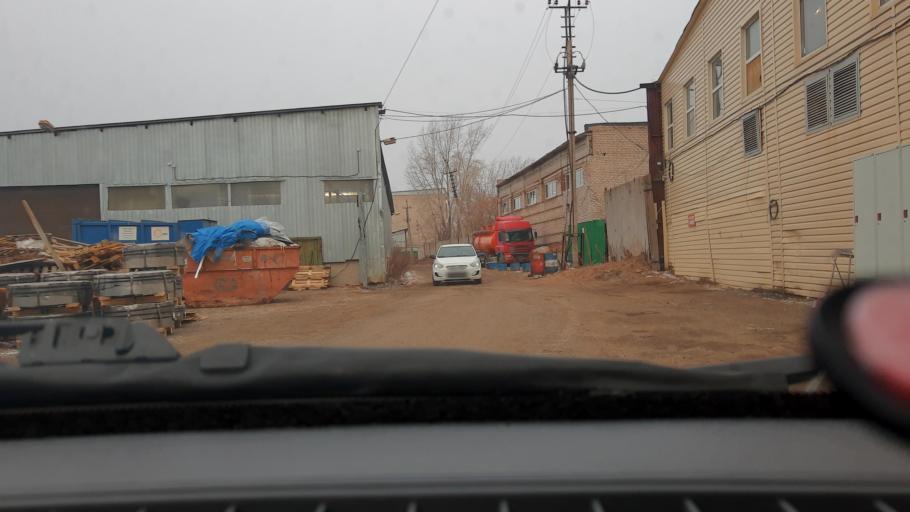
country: RU
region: Bashkortostan
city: Ufa
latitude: 54.7503
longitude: 55.9124
